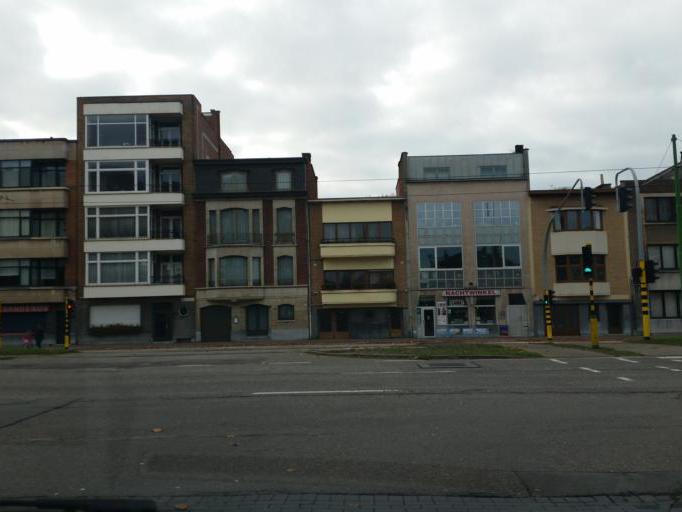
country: BE
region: Flanders
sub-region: Provincie Antwerpen
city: Mortsel
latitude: 51.1866
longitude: 4.4292
